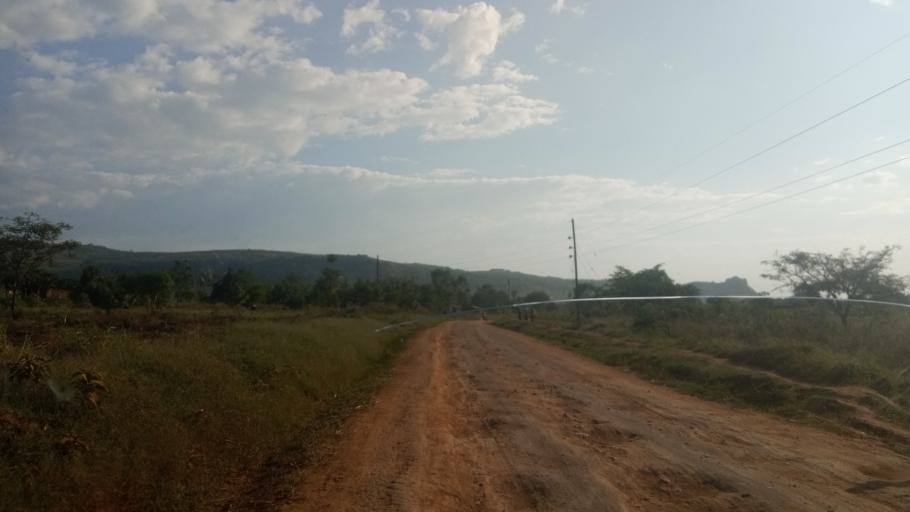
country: UG
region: Eastern Region
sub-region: Kapchorwa District
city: Kapchorwa
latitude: 1.4097
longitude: 34.3476
